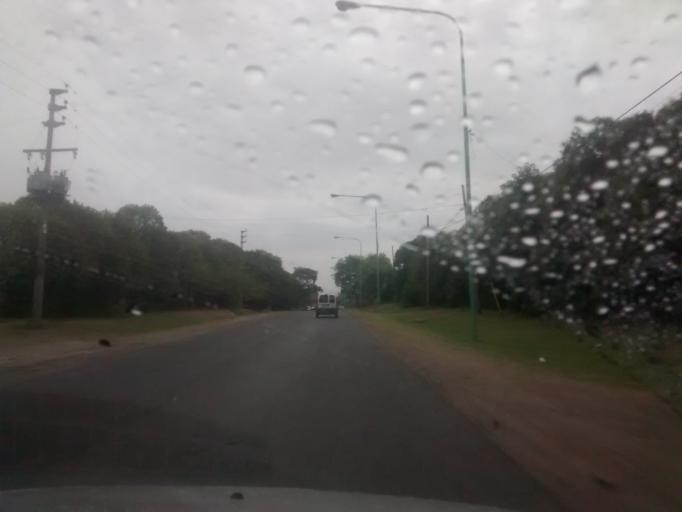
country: AR
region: Buenos Aires
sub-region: Partido de La Plata
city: La Plata
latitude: -34.9089
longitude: -58.0125
